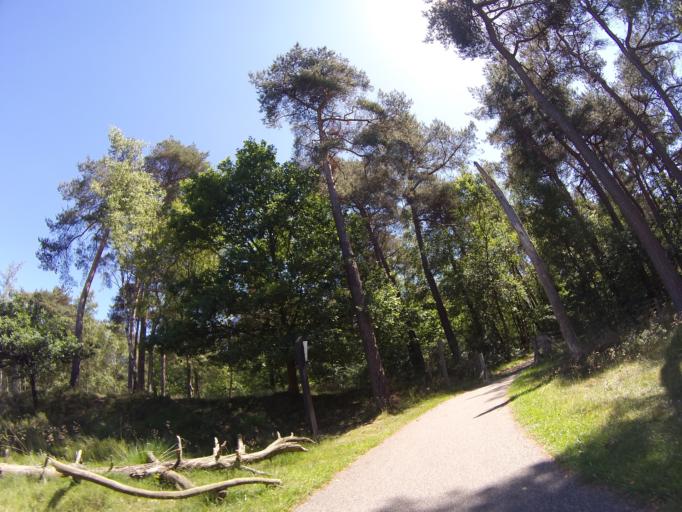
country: NL
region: Drenthe
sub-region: Gemeente Assen
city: Assen
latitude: 52.9262
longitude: 6.5581
